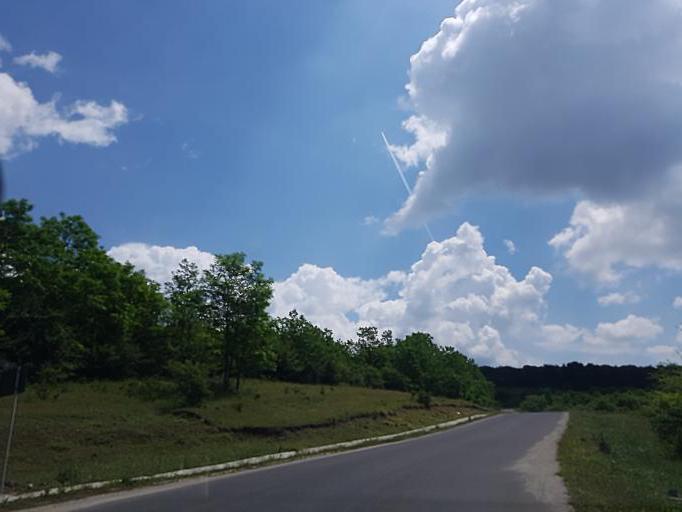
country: RO
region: Sibiu
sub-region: Comuna Seica Mica
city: Seica Mica
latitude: 46.0480
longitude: 24.1556
